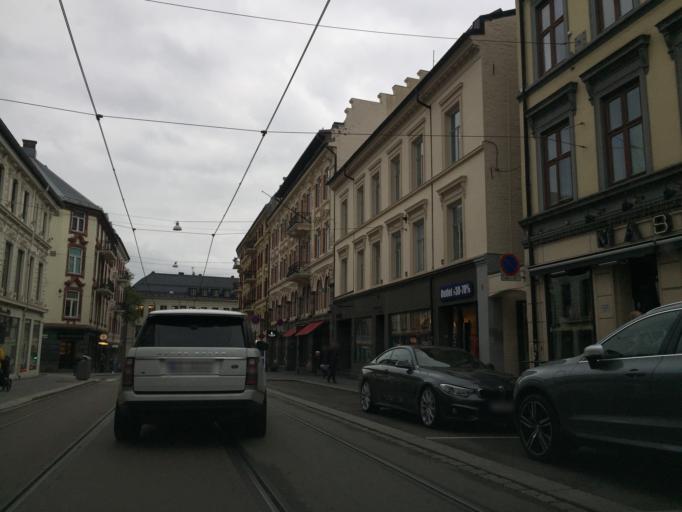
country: NO
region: Oslo
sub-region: Oslo
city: Oslo
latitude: 59.9214
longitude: 10.7273
